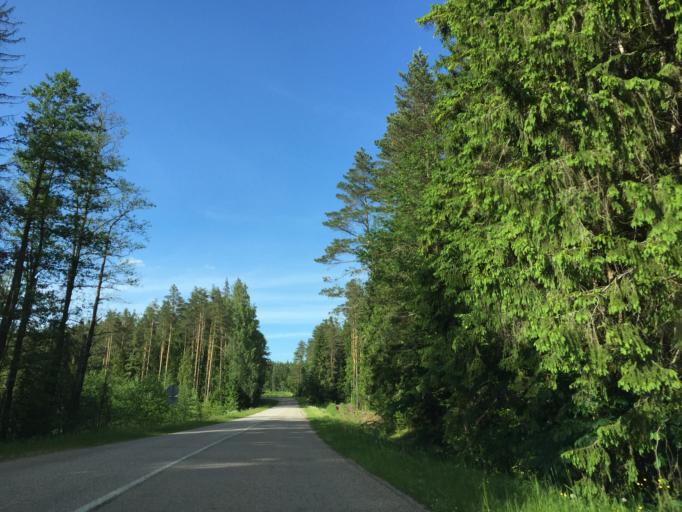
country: LV
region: Preilu Rajons
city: Jaunaglona
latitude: 56.2833
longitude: 27.2118
